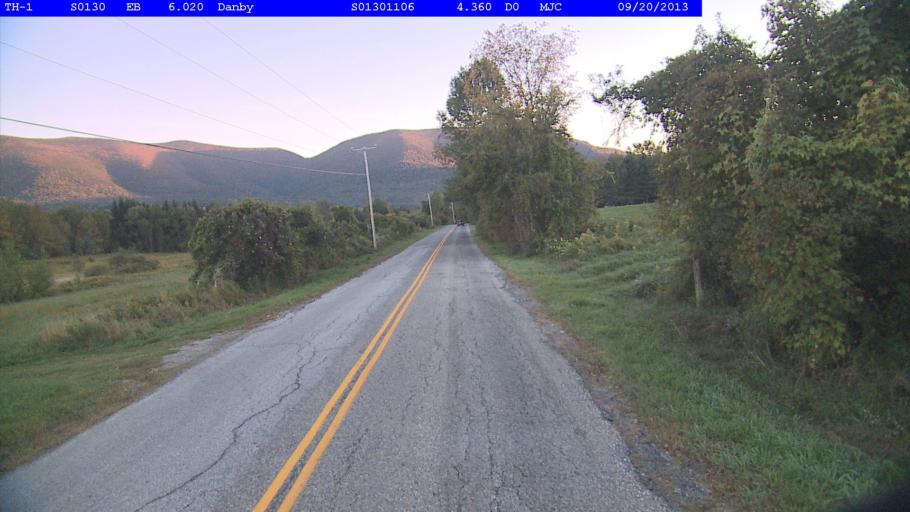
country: US
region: Vermont
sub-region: Bennington County
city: Manchester Center
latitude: 43.3526
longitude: -73.0484
